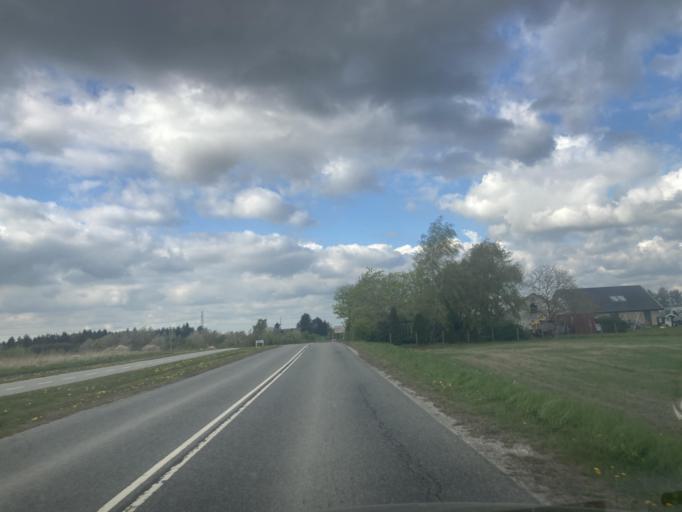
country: DK
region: Zealand
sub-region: Greve Kommune
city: Tune
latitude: 55.6047
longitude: 12.1799
